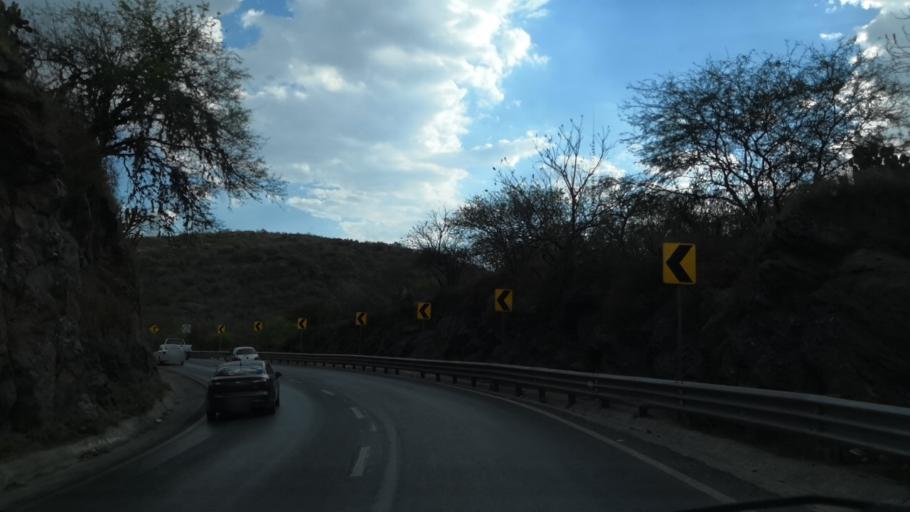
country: MX
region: Guanajuato
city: Marfil
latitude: 21.0030
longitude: -101.2817
